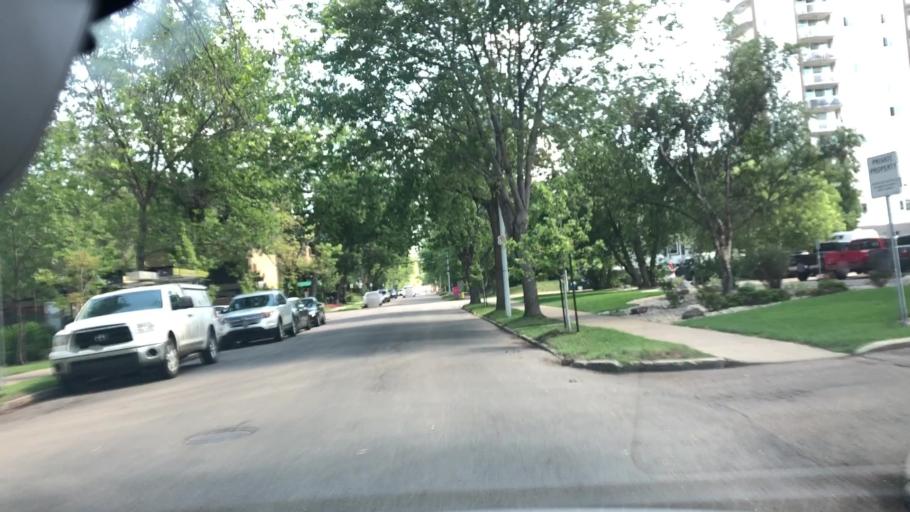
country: CA
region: Alberta
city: Edmonton
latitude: 53.5373
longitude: -113.5169
